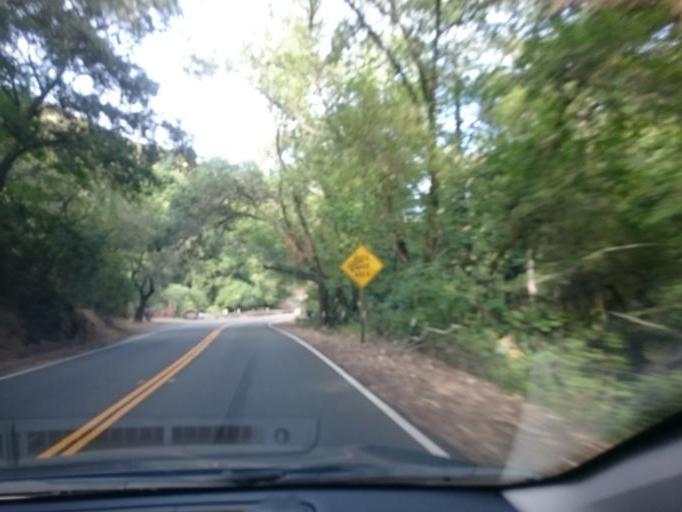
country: US
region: California
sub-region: Napa County
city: Yountville
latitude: 38.4877
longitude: -122.3101
